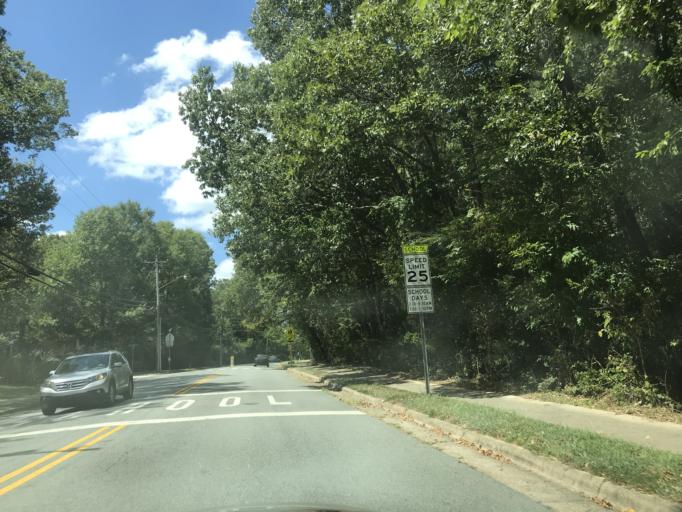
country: US
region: North Carolina
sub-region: Orange County
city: Chapel Hill
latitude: 35.9325
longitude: -79.0144
